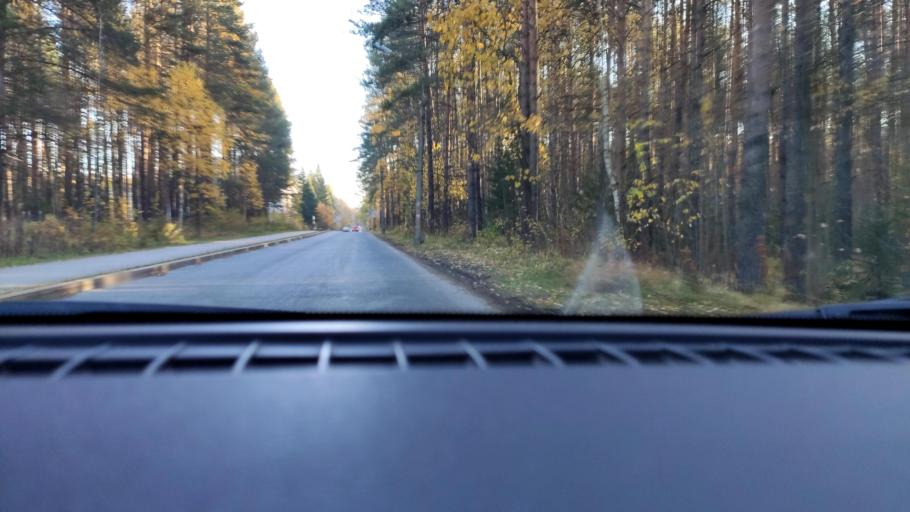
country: RU
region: Perm
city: Perm
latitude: 58.0528
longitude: 56.2284
